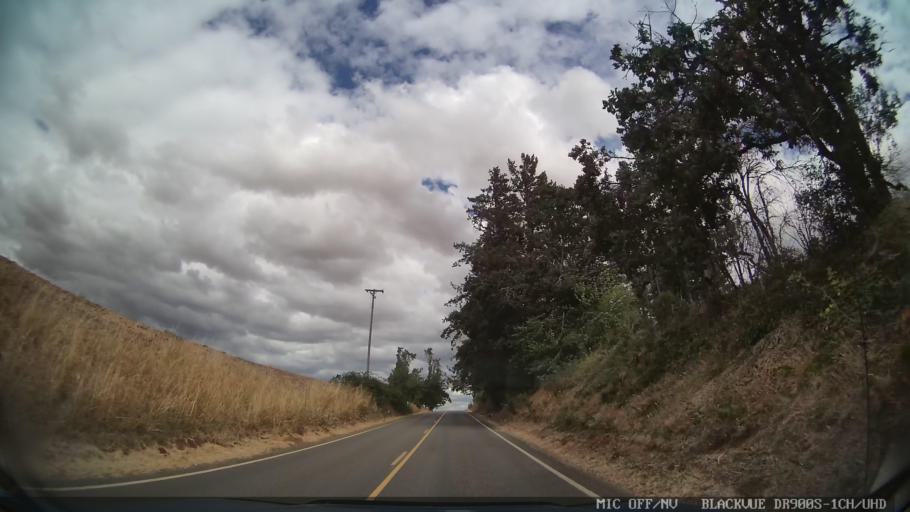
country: US
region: Oregon
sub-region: Marion County
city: Sublimity
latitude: 44.8654
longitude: -122.8174
